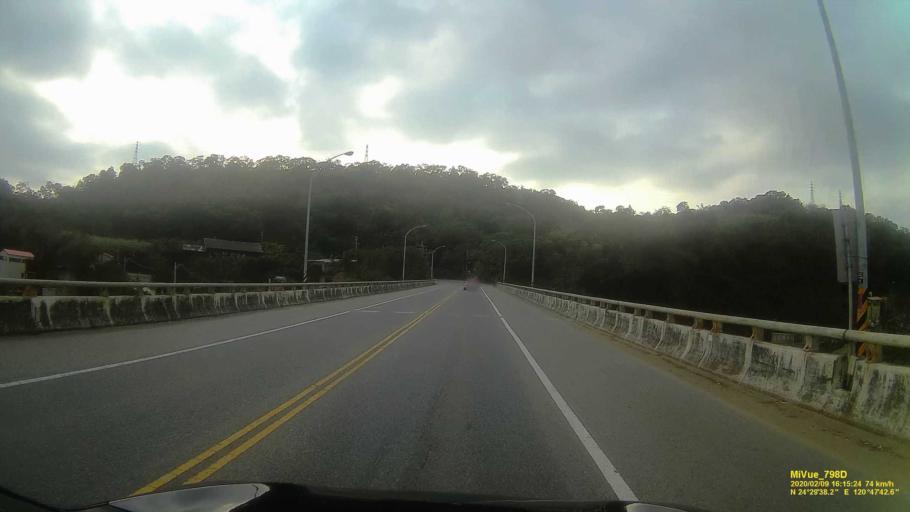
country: TW
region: Taiwan
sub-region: Miaoli
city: Miaoli
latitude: 24.4939
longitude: 120.7949
